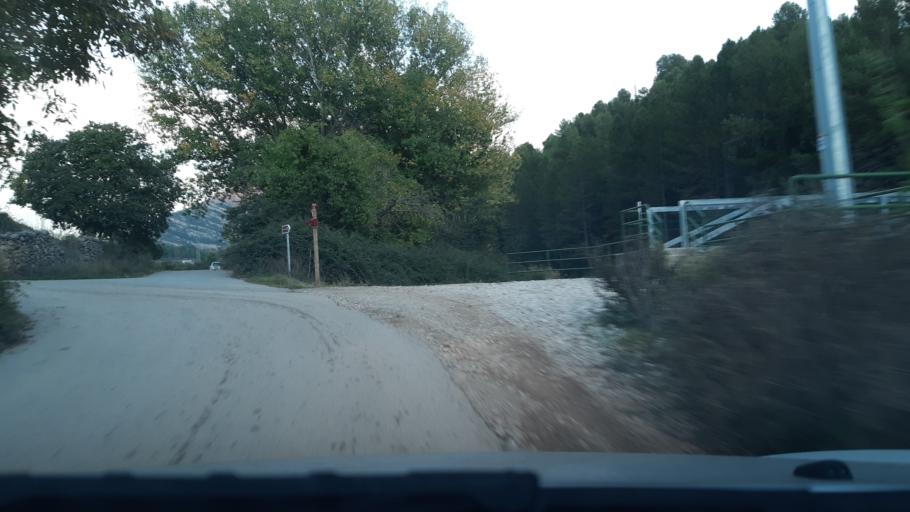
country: ES
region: Aragon
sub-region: Provincia de Teruel
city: Valderrobres
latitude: 40.8403
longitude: 0.1974
